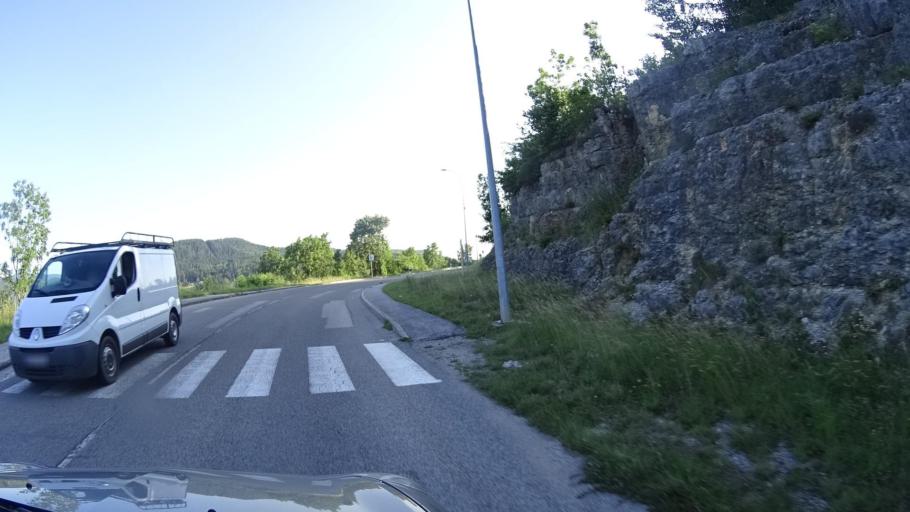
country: FR
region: Franche-Comte
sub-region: Departement du Jura
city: Morbier
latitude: 46.5385
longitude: 6.0137
